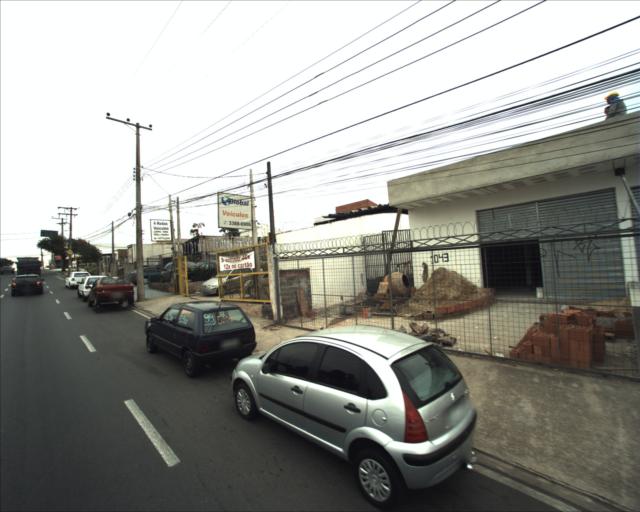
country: BR
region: Sao Paulo
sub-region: Sorocaba
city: Sorocaba
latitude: -23.4900
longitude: -47.5018
